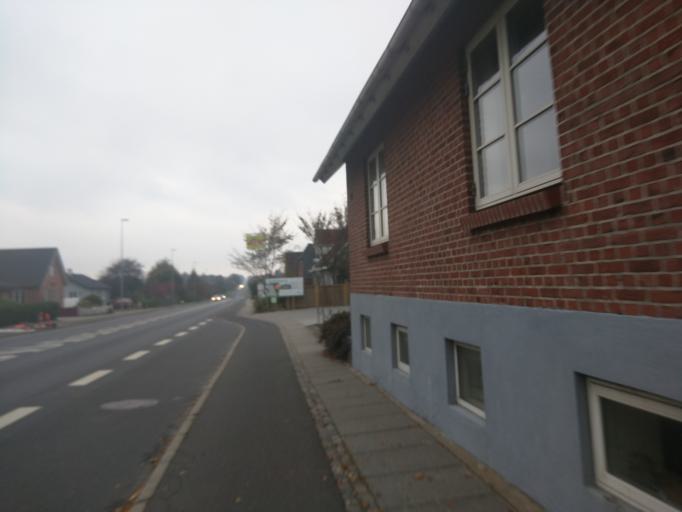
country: DK
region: Central Jutland
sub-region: Silkeborg Kommune
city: Silkeborg
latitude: 56.2132
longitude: 9.5023
